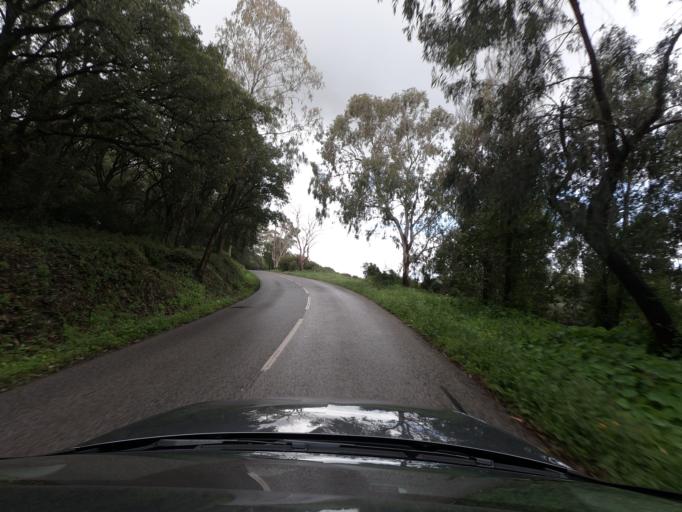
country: PT
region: Lisbon
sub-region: Sintra
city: Queluz
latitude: 38.7438
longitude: -9.2629
